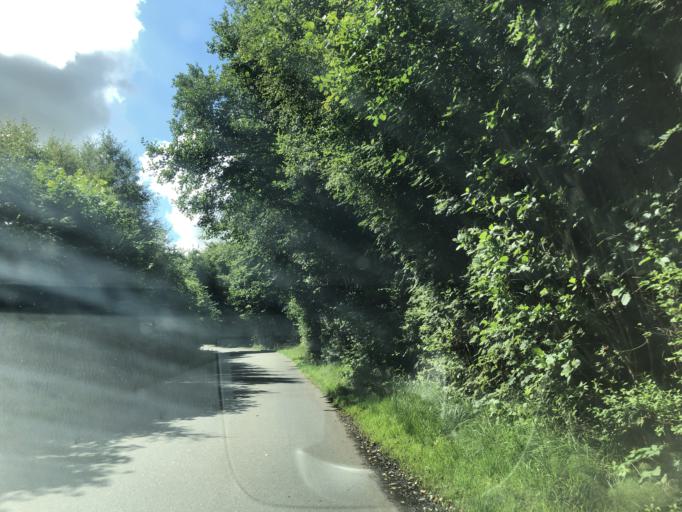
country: DK
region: Central Jutland
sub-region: Struer Kommune
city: Struer
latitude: 56.4797
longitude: 8.5219
